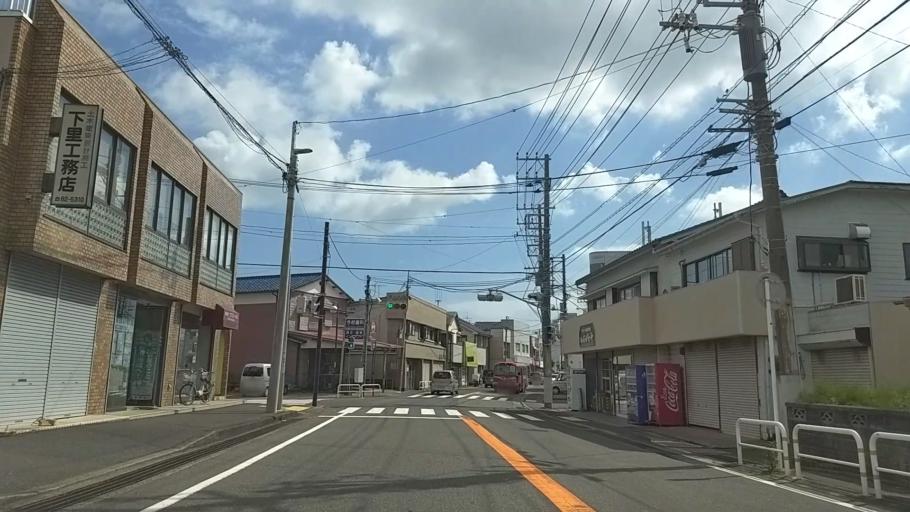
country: JP
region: Kanagawa
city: Miura
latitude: 35.1496
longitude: 139.6279
